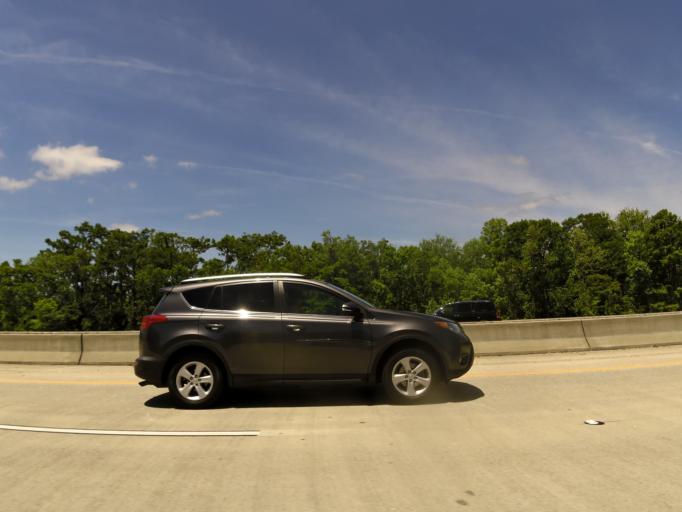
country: US
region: Georgia
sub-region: McIntosh County
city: Darien
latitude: 31.3675
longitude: -81.4567
